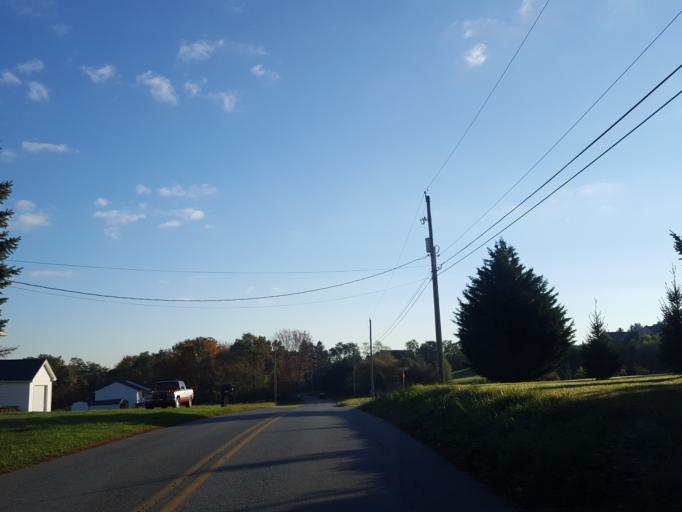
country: US
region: Pennsylvania
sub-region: York County
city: Yoe
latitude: 39.9457
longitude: -76.6331
